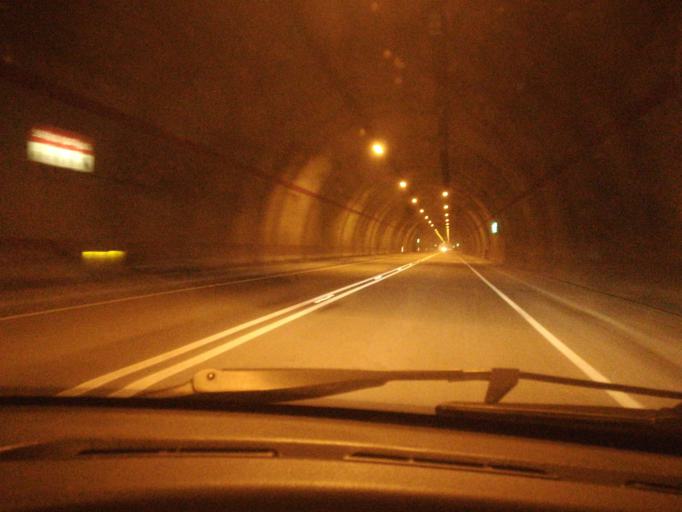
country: IT
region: The Marches
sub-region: Provincia di Macerata
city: Macerata
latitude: 43.2984
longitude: 13.4416
